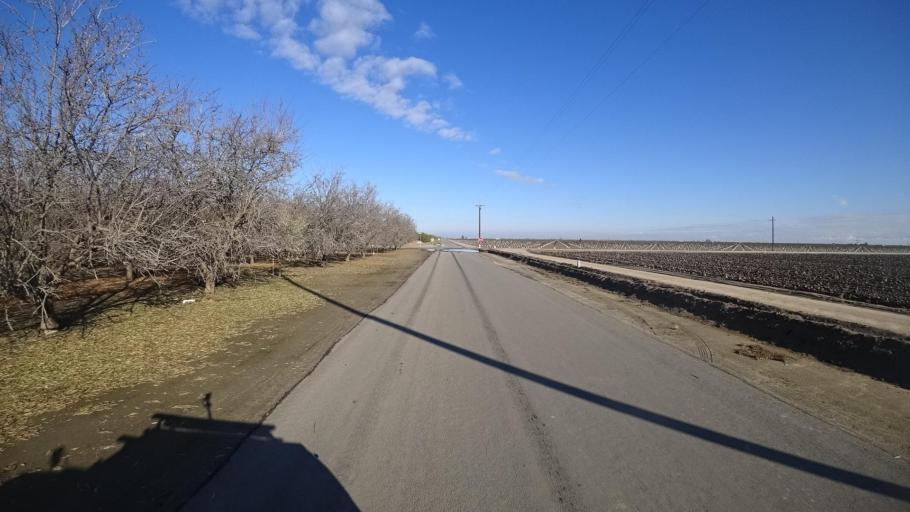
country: US
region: California
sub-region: Kern County
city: McFarland
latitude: 35.7024
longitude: -119.2936
